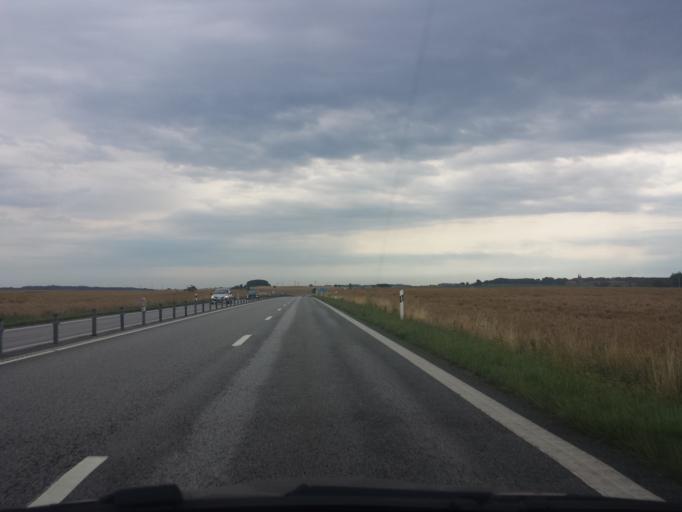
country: SE
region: Skane
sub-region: Skurups Kommun
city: Rydsgard
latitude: 55.4729
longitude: 13.6811
